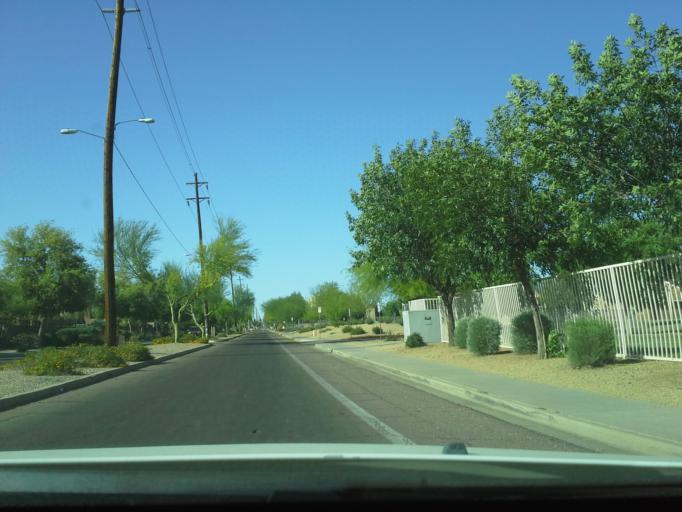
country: US
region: Arizona
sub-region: Maricopa County
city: Glendale
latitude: 33.5347
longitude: -112.2117
